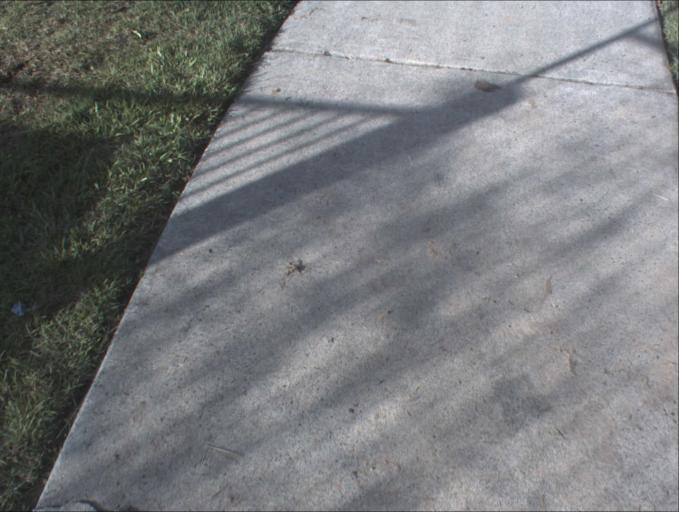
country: AU
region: Queensland
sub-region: Logan
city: North Maclean
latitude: -27.8063
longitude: 152.9523
